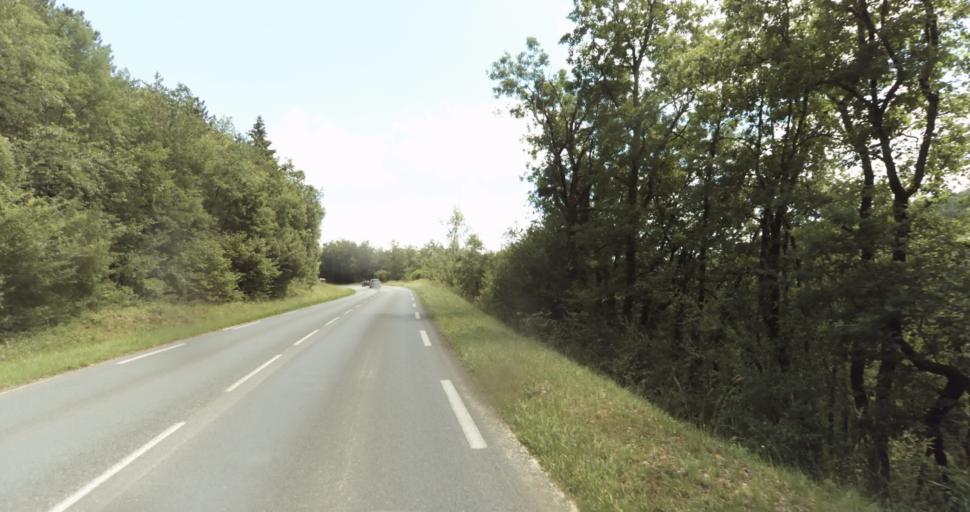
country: FR
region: Aquitaine
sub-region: Departement de la Dordogne
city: Lalinde
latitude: 44.8454
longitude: 0.8239
